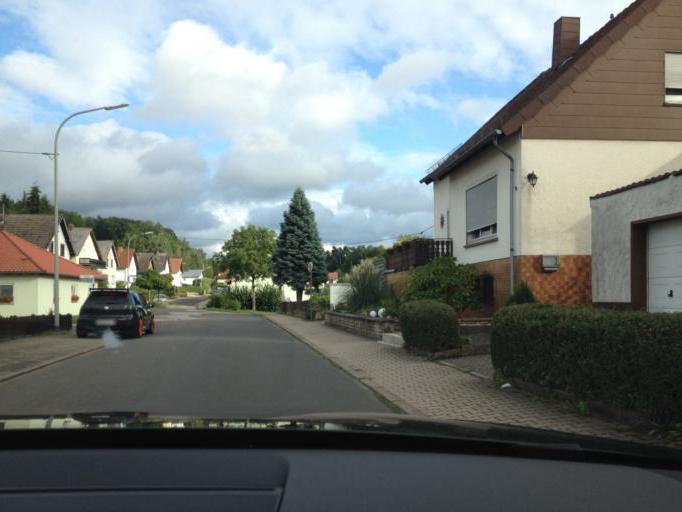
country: DE
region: Saarland
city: Namborn
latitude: 49.5183
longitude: 7.1406
